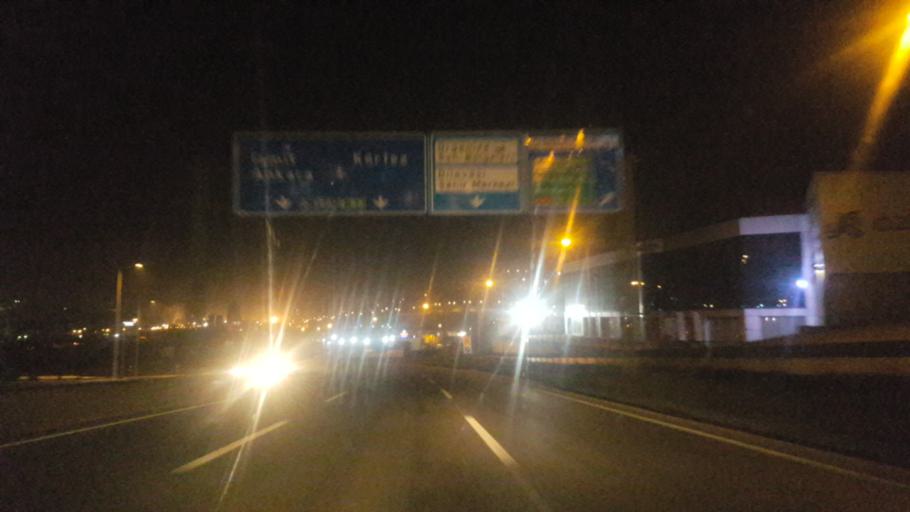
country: TR
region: Kocaeli
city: Tavsanli
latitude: 40.7943
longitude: 29.5266
